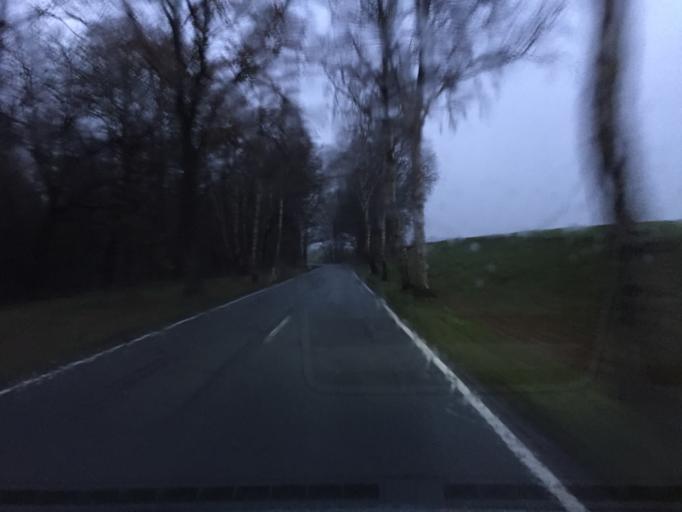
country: DE
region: Lower Saxony
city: Sudwalde
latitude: 52.8518
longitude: 8.8492
